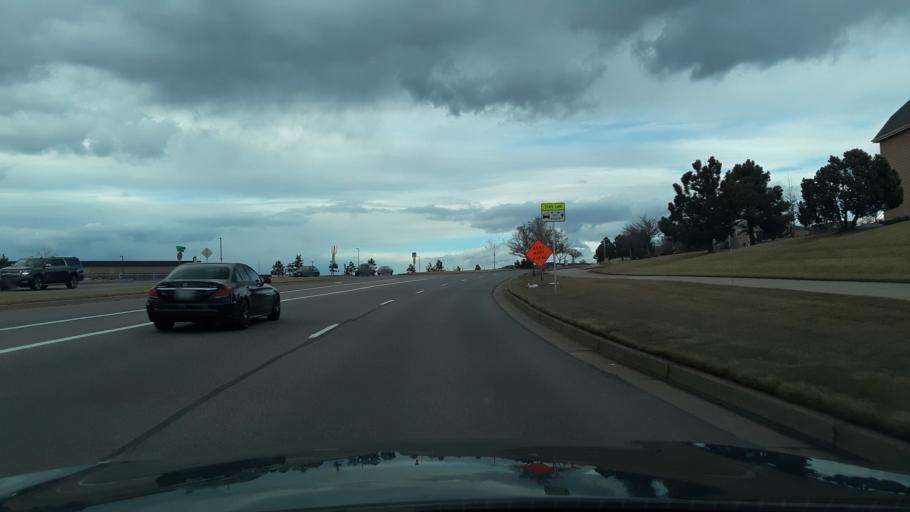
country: US
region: Colorado
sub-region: El Paso County
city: Gleneagle
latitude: 39.0121
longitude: -104.8089
